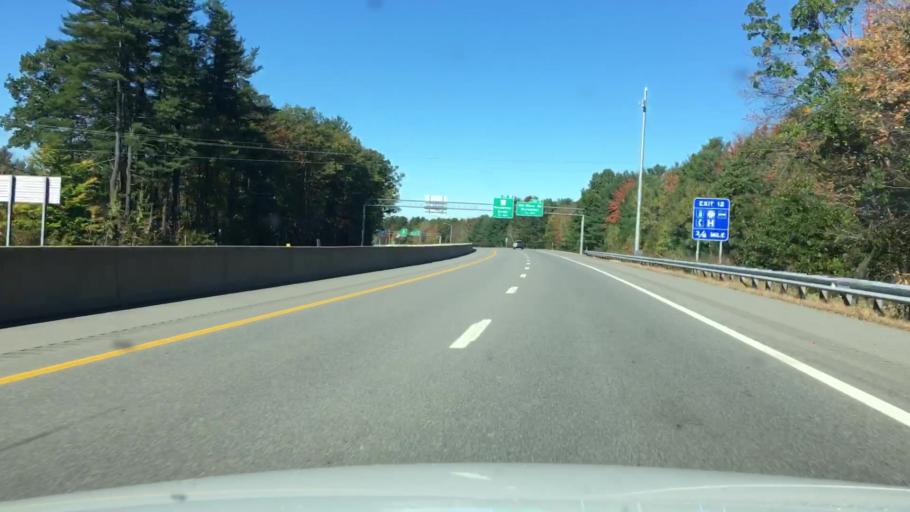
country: US
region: New Hampshire
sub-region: Strafford County
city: Rochester
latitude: 43.2774
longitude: -70.9677
